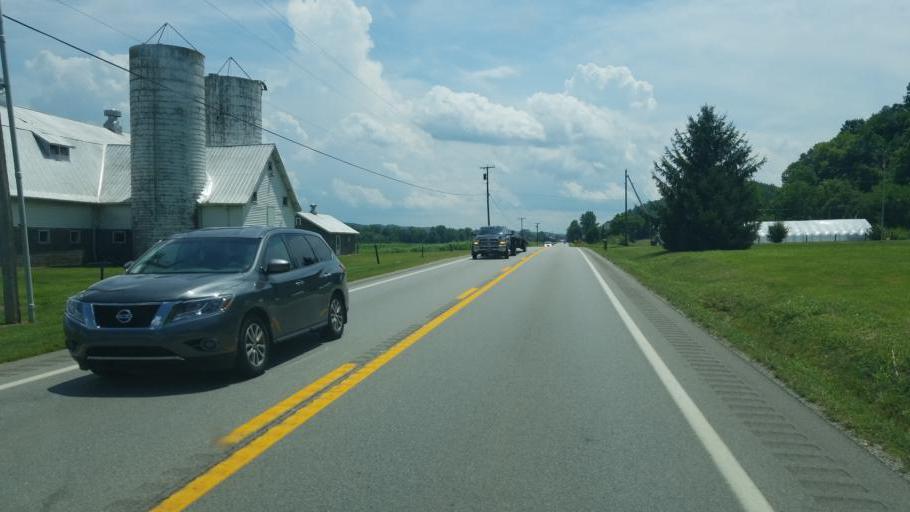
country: US
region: West Virginia
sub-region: Putnam County
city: Buffalo
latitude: 38.7274
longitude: -81.9721
